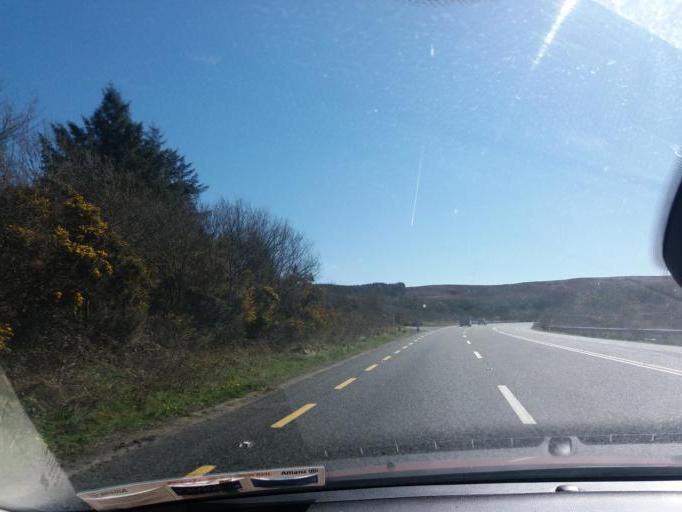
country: IE
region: Munster
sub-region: County Cork
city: Millstreet
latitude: 51.9805
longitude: -9.2588
